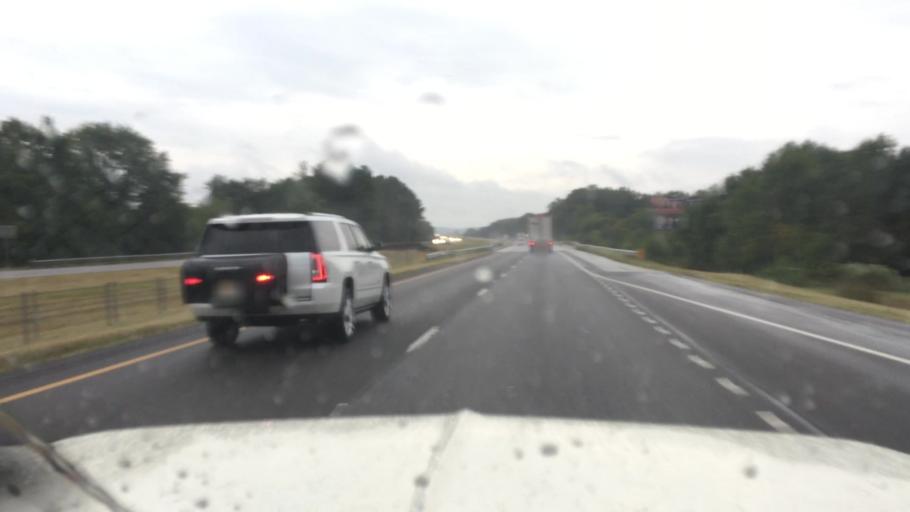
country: US
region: Alabama
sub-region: Morgan County
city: Falkville
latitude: 34.4079
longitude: -86.8983
